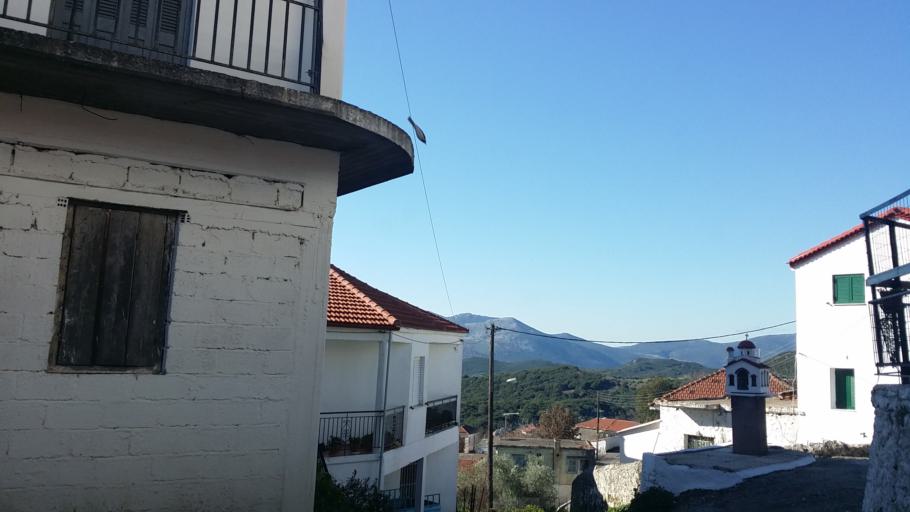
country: GR
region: West Greece
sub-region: Nomos Aitolias kai Akarnanias
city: Fitiai
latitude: 38.7094
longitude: 21.1734
